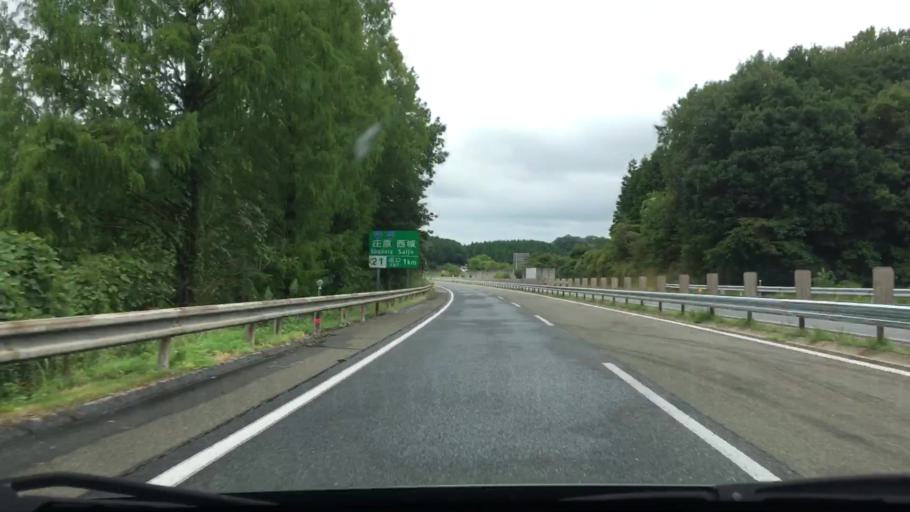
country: JP
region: Hiroshima
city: Shobara
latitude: 34.8426
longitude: 133.0383
